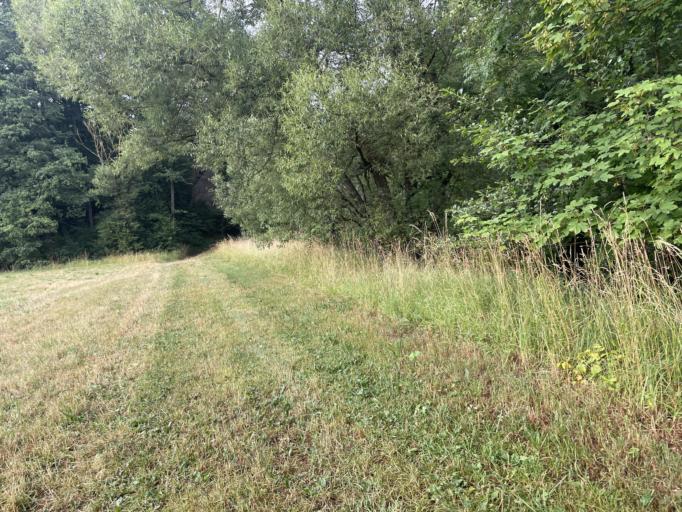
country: DE
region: Bavaria
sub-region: Upper Franconia
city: Neunkirchen am Main
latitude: 49.9359
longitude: 11.6272
